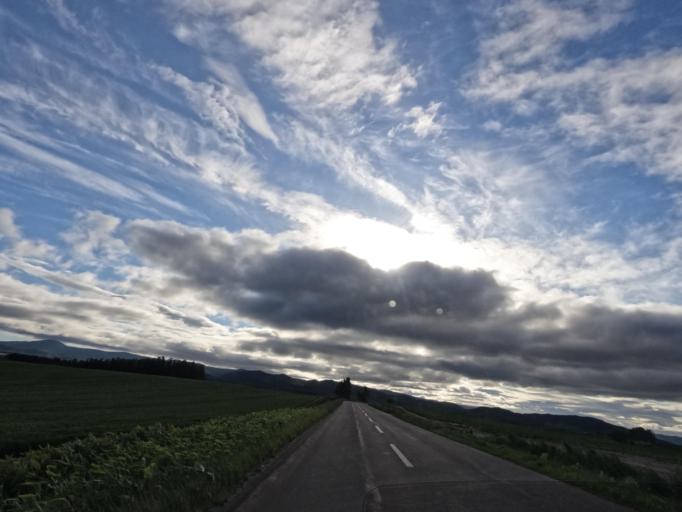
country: JP
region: Hokkaido
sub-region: Asahikawa-shi
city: Asahikawa
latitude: 43.6265
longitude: 142.4355
